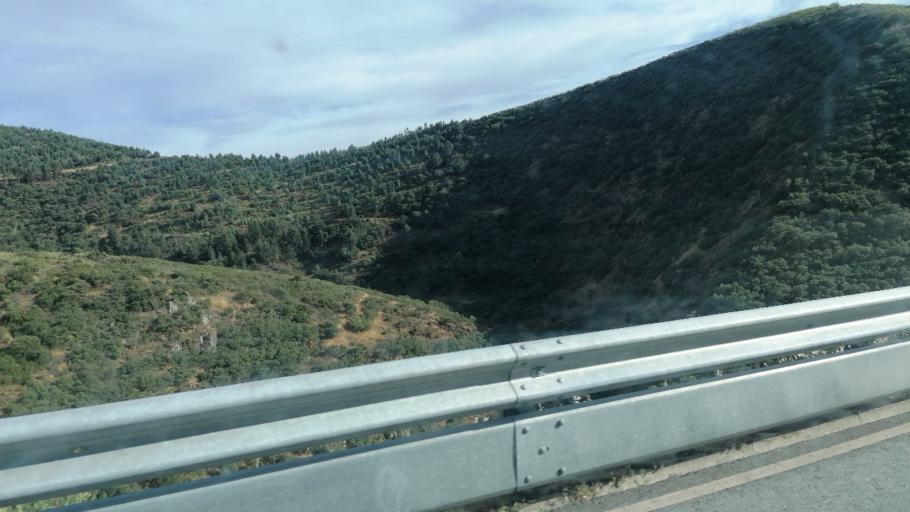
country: PT
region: Viseu
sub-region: Sao Joao da Pesqueira
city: Sao Joao da Pesqueira
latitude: 41.1193
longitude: -7.4451
